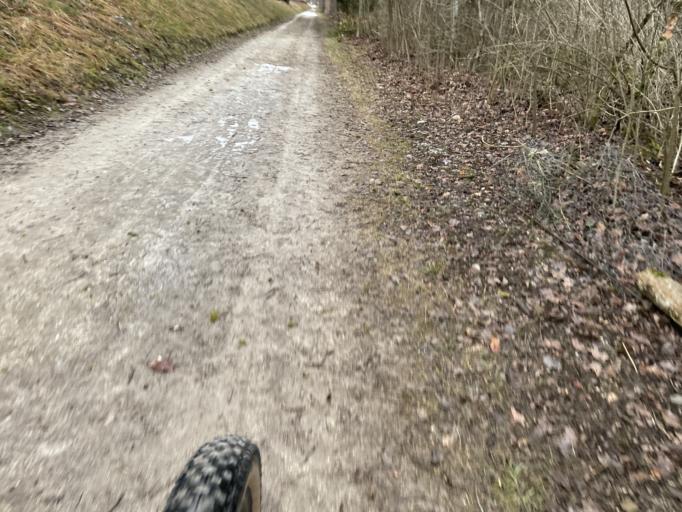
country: CH
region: Bern
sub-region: Bern-Mittelland District
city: Munsingen
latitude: 46.8574
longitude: 7.5541
